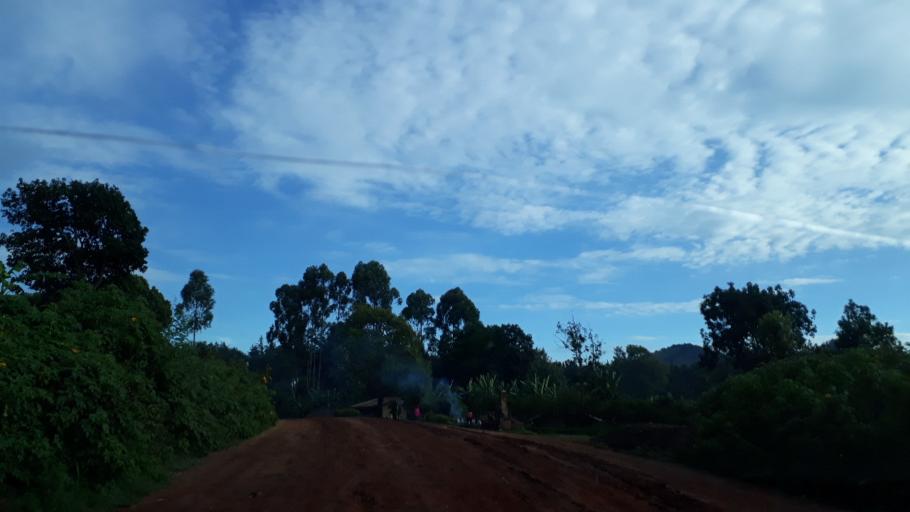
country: UG
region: Northern Region
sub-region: Zombo District
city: Paidha
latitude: 2.2455
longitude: 30.8624
